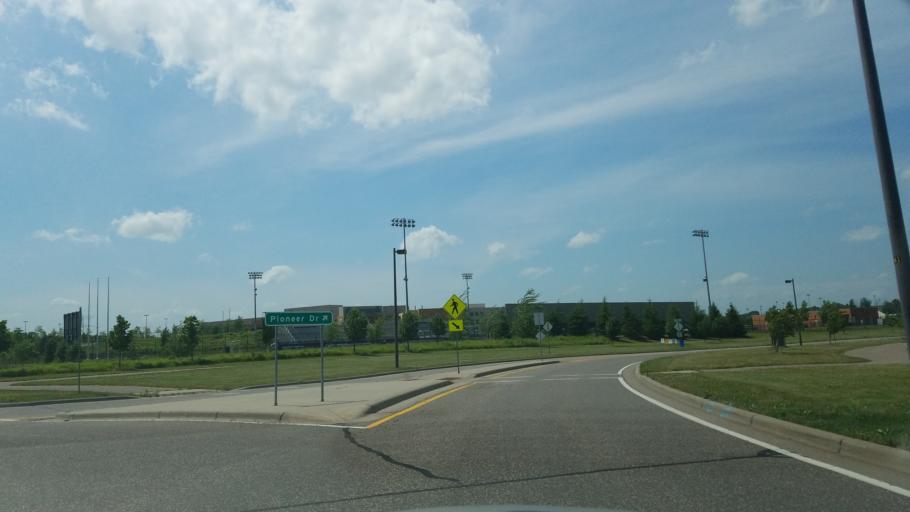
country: US
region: Minnesota
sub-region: Washington County
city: Woodbury
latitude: 44.8854
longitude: -92.9273
